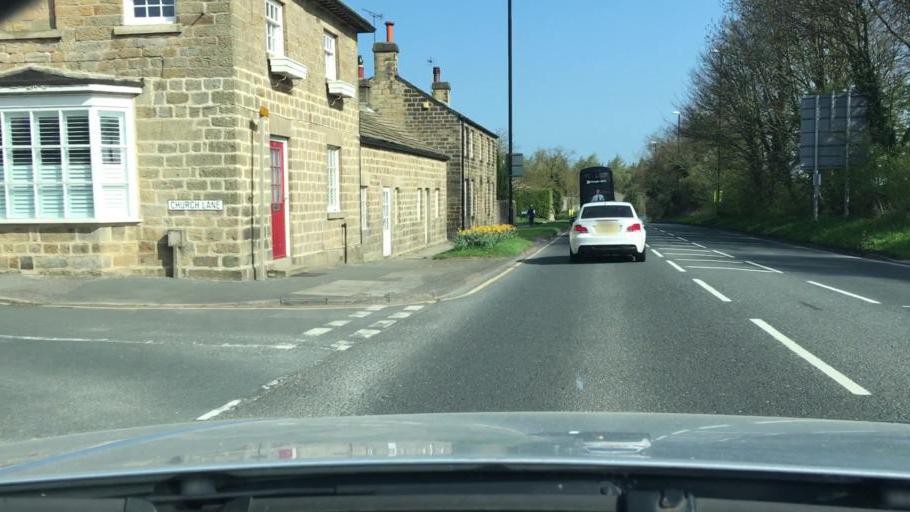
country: GB
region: England
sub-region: City and Borough of Leeds
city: East Keswick
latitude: 53.9019
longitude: -1.5120
